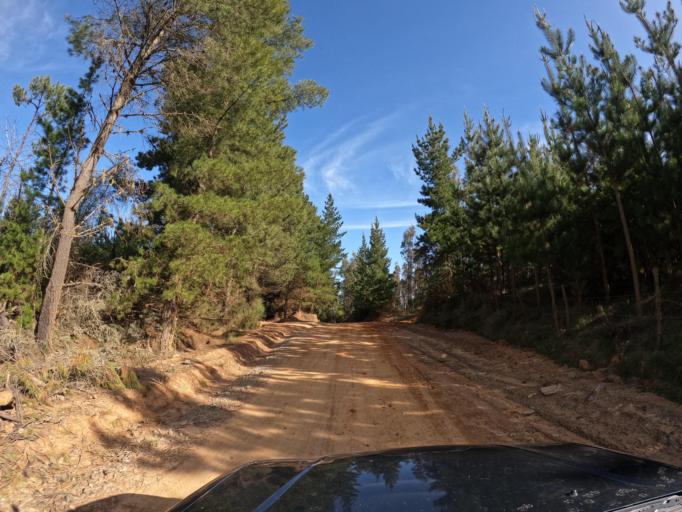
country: CL
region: Biobio
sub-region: Provincia de Biobio
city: La Laja
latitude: -37.1158
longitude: -72.7391
